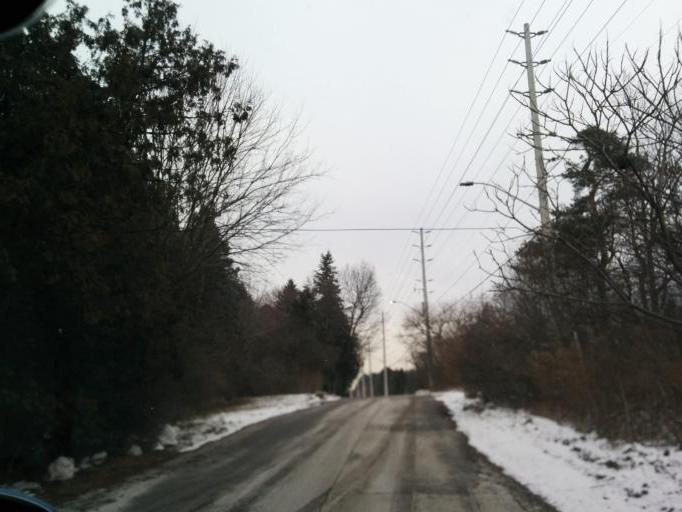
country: CA
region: Ontario
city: Mississauga
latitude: 43.5382
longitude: -79.6481
